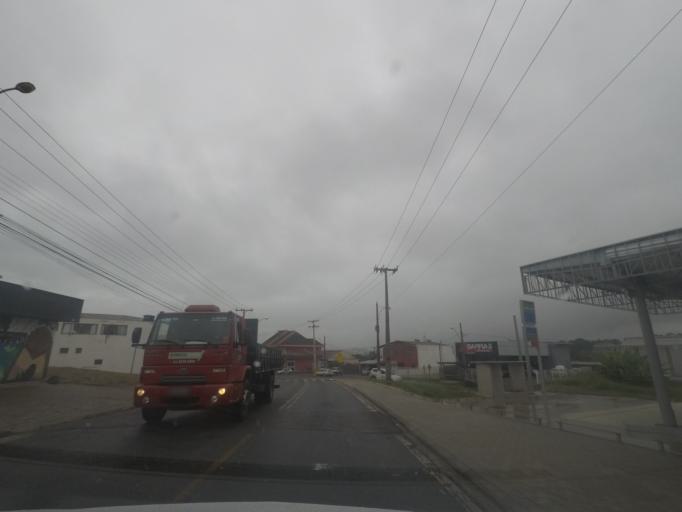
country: BR
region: Parana
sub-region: Quatro Barras
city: Quatro Barras
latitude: -25.3699
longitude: -49.0809
